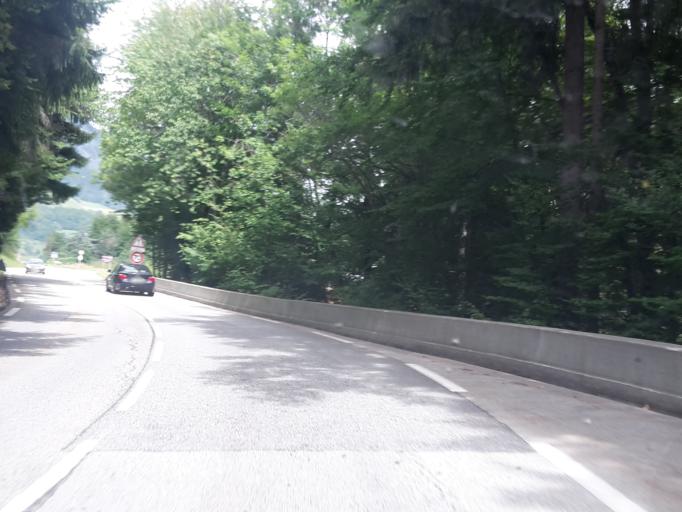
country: FR
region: Rhone-Alpes
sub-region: Departement de la Haute-Savoie
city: Praz-sur-Arly
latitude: 45.8062
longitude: 6.5025
